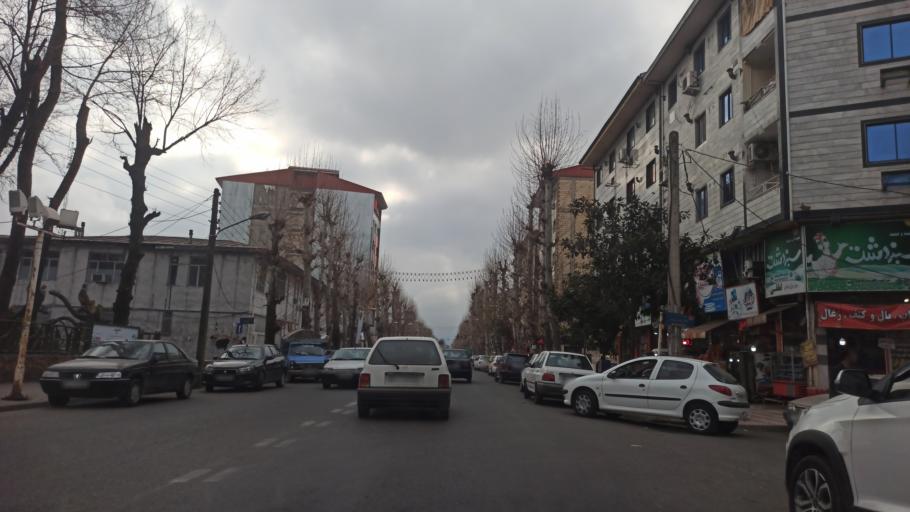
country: IR
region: Gilan
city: Fuman
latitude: 37.2310
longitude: 49.3175
